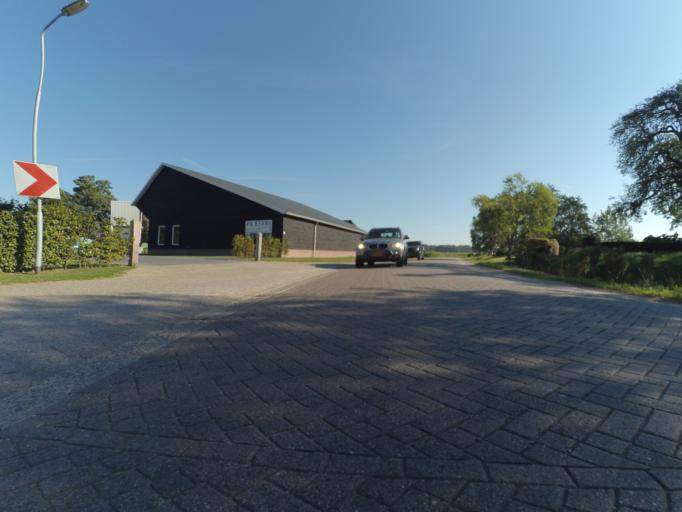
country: NL
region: Gelderland
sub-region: Gemeente Ermelo
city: Horst
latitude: 52.2694
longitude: 5.5504
